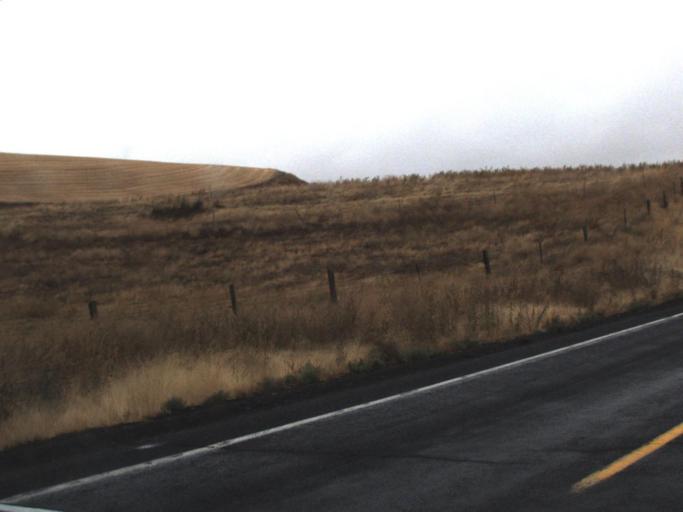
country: US
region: Washington
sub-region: Whitman County
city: Colfax
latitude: 47.1116
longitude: -117.6380
